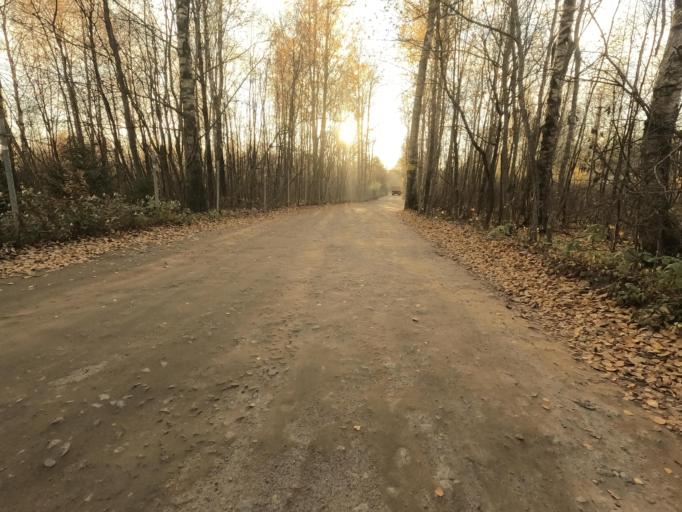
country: RU
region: St.-Petersburg
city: Beloostrov
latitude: 60.1816
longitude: 30.0472
